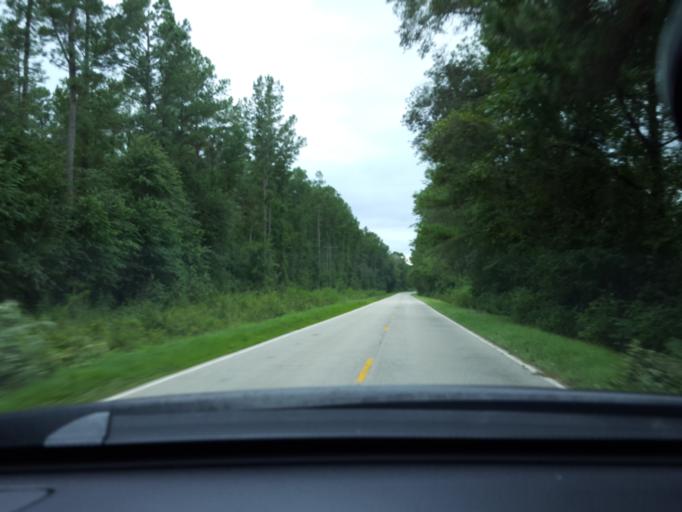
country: US
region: North Carolina
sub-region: Sampson County
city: Clinton
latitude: 34.7937
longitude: -78.3061
